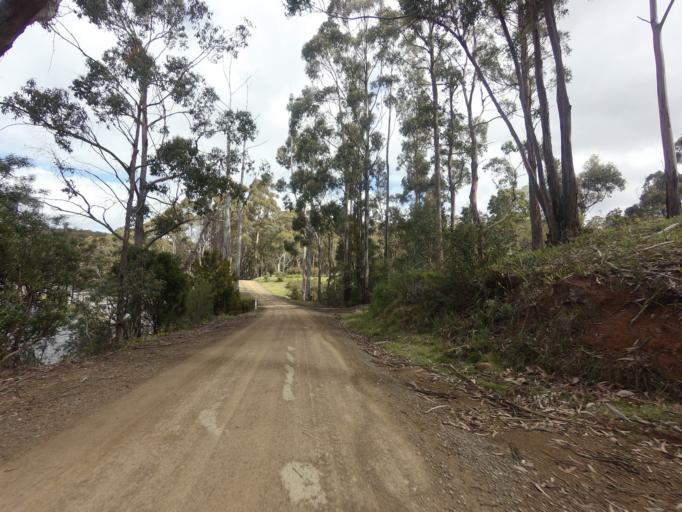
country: AU
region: Tasmania
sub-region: Huon Valley
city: Geeveston
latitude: -43.4207
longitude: 147.0128
